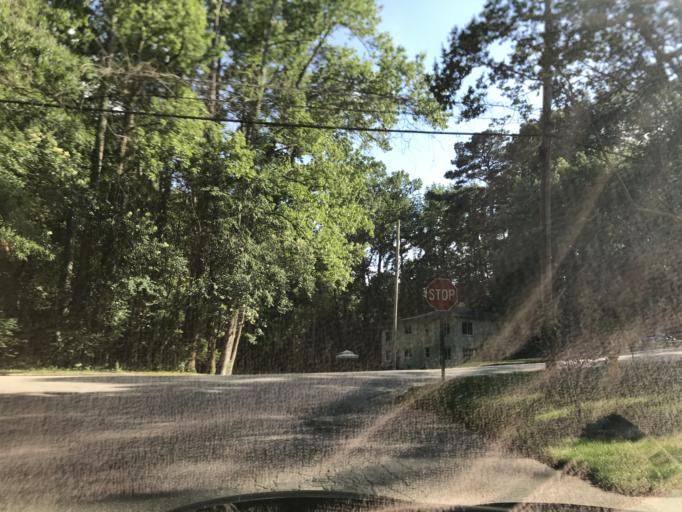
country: US
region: North Carolina
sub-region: Wake County
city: West Raleigh
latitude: 35.8047
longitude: -78.6749
